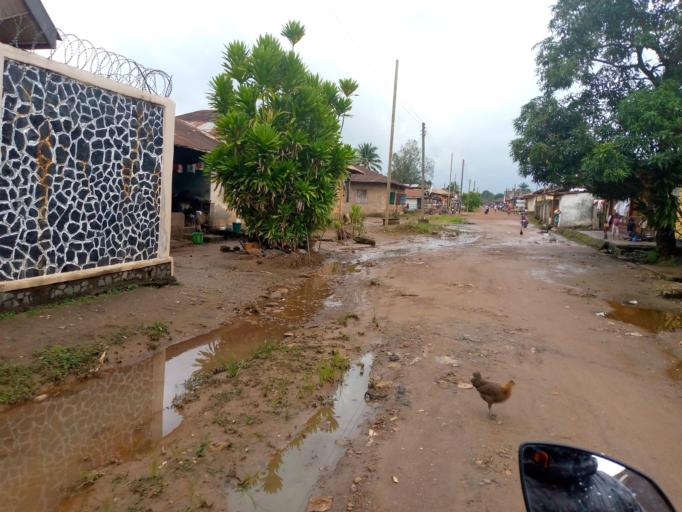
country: SL
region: Eastern Province
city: Kenema
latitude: 7.8869
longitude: -11.1862
